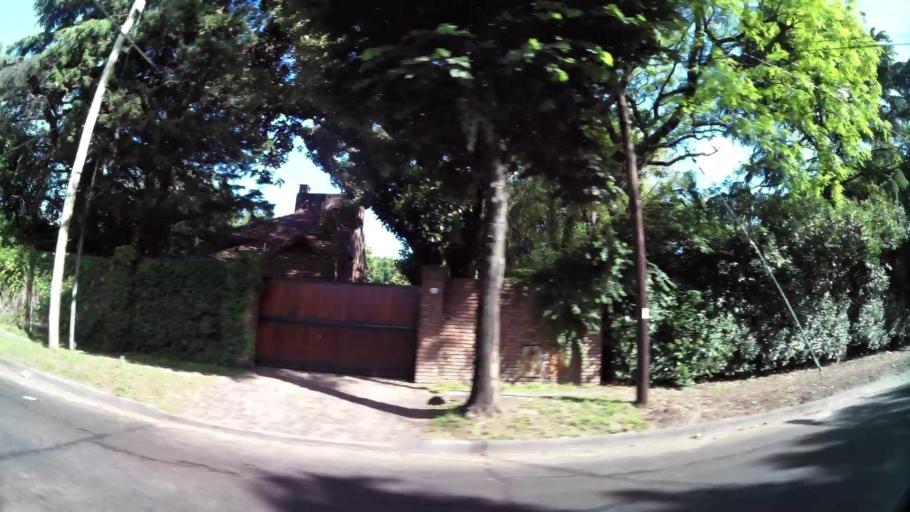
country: AR
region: Buenos Aires
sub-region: Partido de San Isidro
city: San Isidro
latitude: -34.4848
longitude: -58.5628
